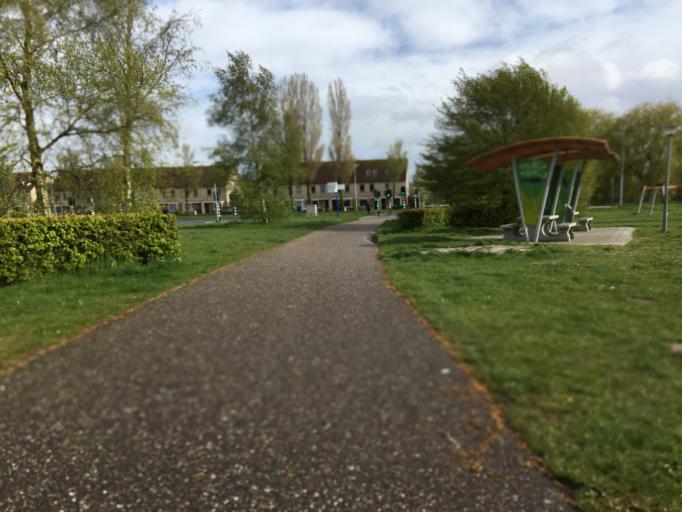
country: NL
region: Flevoland
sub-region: Gemeente Almere
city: Almere Stad
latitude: 52.3644
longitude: 5.2561
